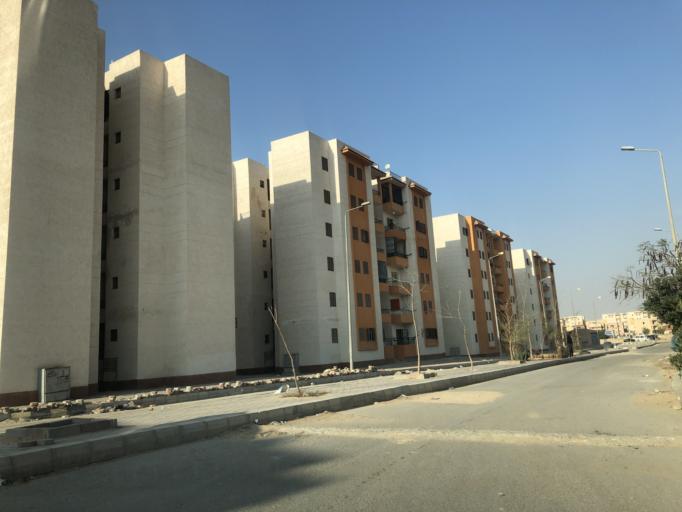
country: EG
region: Al Jizah
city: Madinat Sittah Uktubar
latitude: 29.9055
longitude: 30.9280
